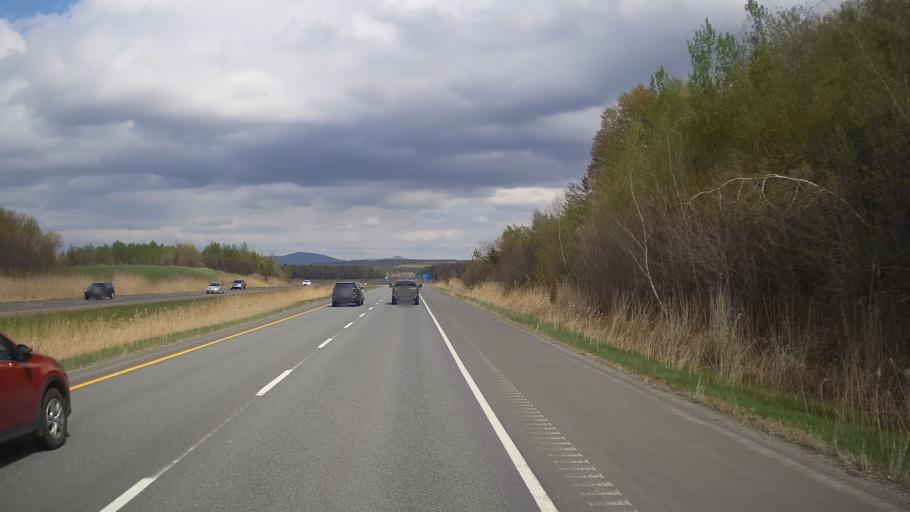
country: CA
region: Quebec
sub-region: Monteregie
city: Granby
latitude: 45.3483
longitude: -72.8186
